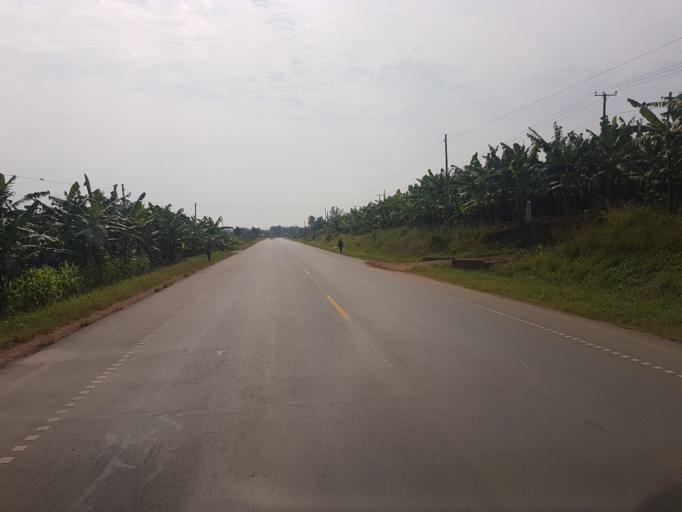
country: UG
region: Western Region
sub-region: Sheema District
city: Kibingo
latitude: -0.6368
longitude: 30.5163
